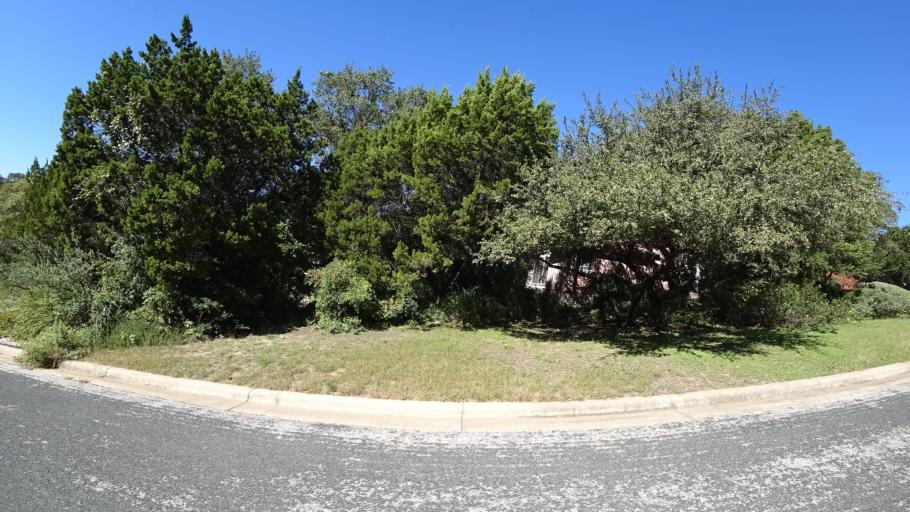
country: US
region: Texas
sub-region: Travis County
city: West Lake Hills
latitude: 30.3451
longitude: -97.7767
